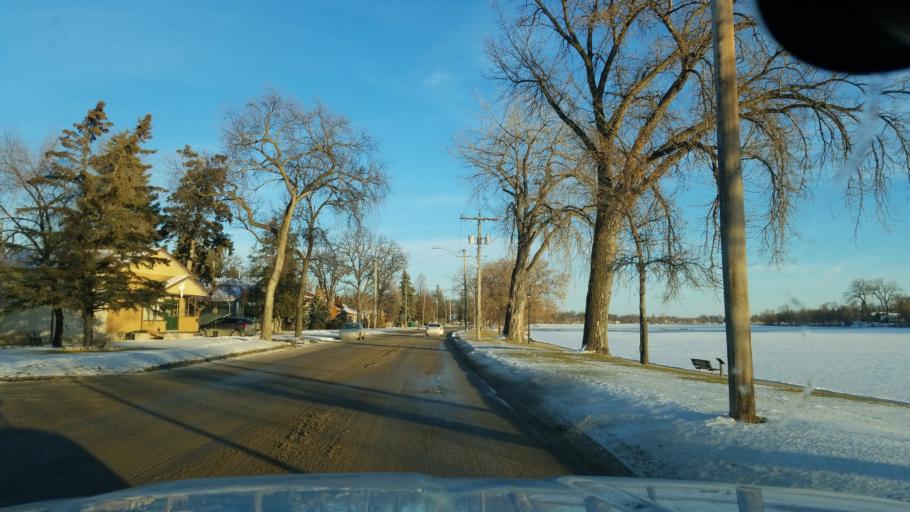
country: CA
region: Manitoba
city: Portage la Prairie
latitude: 49.9703
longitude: -98.3067
